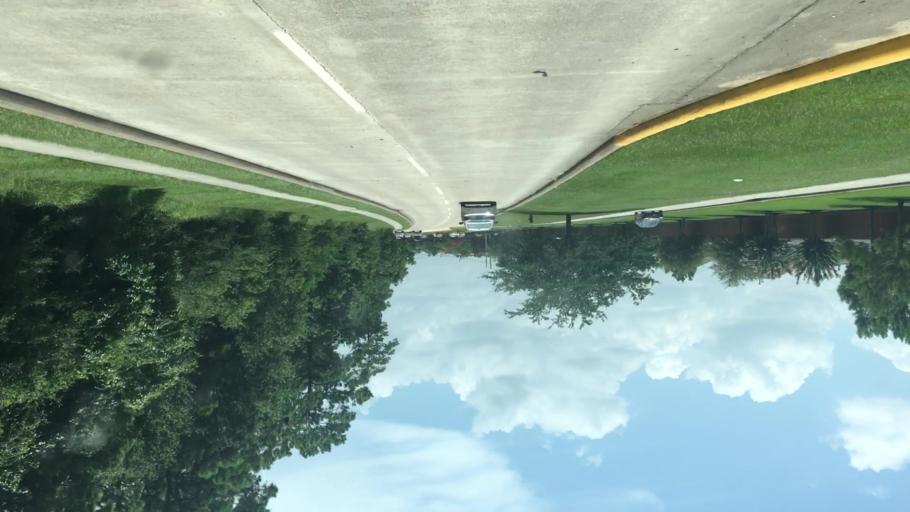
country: US
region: Texas
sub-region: Harris County
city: Atascocita
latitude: 29.9783
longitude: -95.2006
